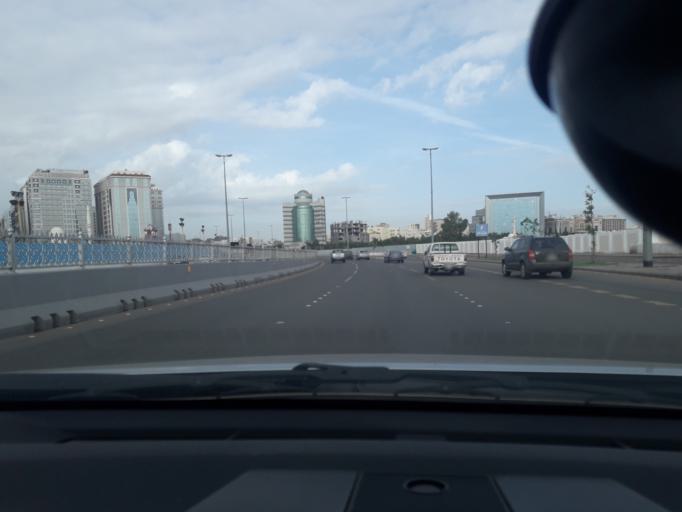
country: SA
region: Al Madinah al Munawwarah
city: Medina
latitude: 24.4724
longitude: 39.6175
